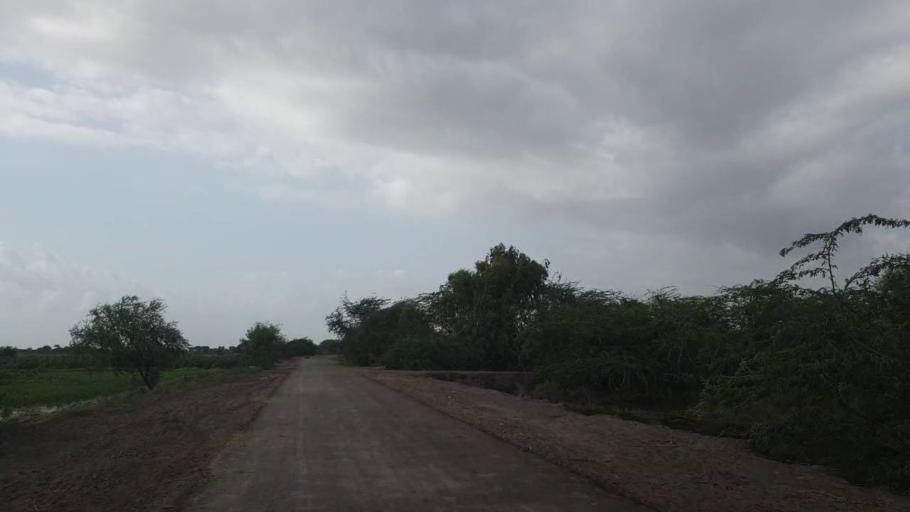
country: PK
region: Sindh
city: Kadhan
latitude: 24.5971
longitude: 69.0569
